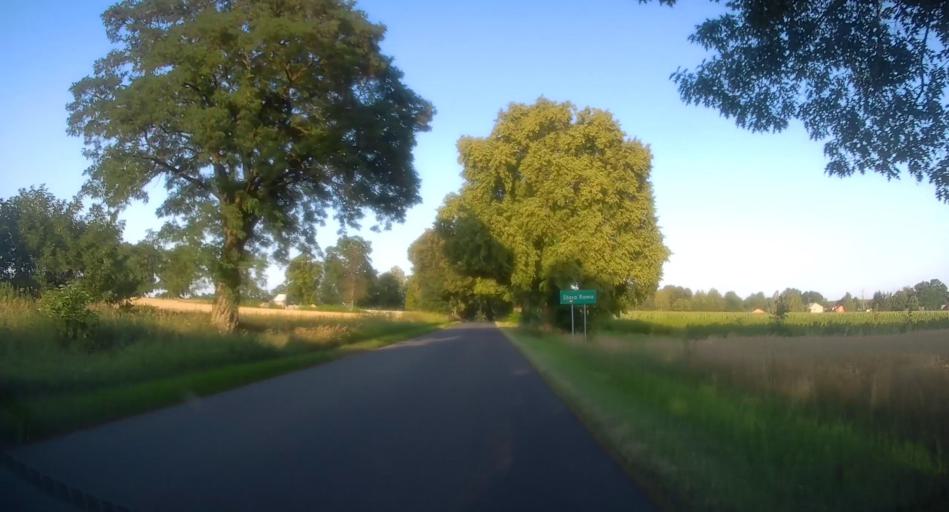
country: PL
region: Lodz Voivodeship
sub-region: Powiat skierniewicki
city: Kaweczyn Nowy
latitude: 51.8837
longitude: 20.2659
